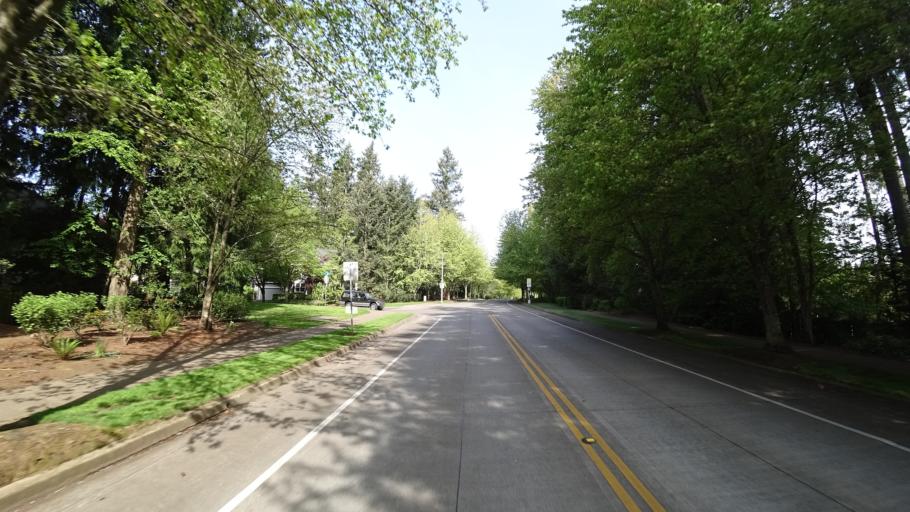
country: US
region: Oregon
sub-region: Washington County
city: Aloha
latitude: 45.4450
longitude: -122.8409
